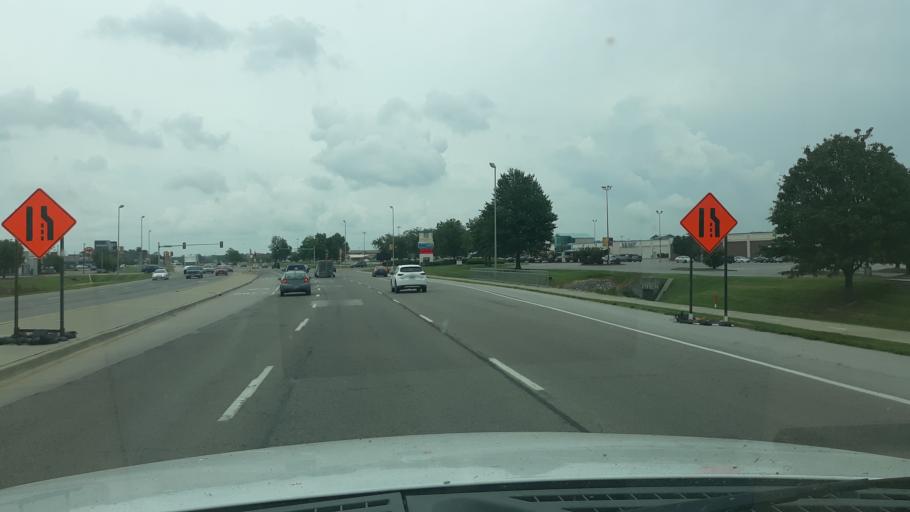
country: US
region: Illinois
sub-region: Jackson County
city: Carbondale
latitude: 37.7291
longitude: -89.1955
